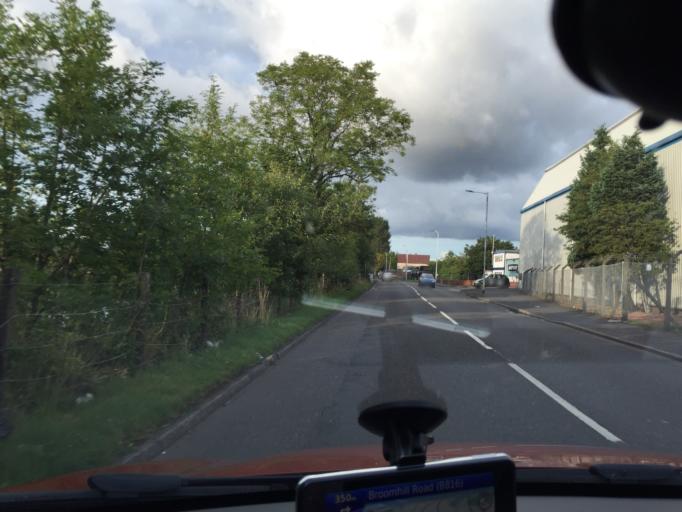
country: GB
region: Scotland
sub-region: Falkirk
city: Bonnybridge
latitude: 55.9974
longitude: -3.8911
